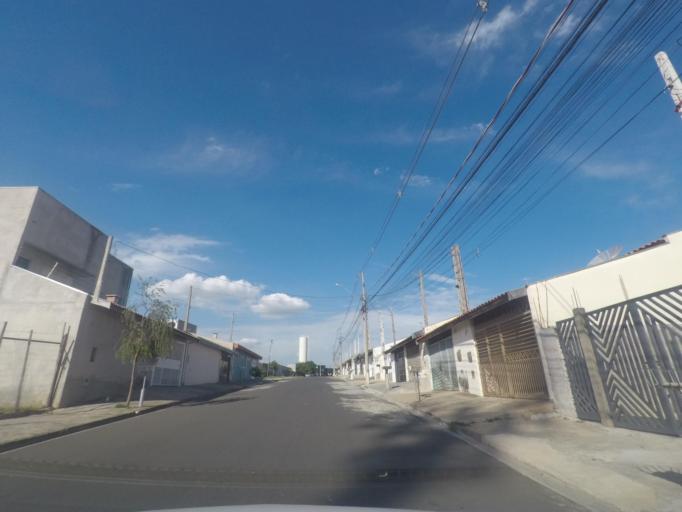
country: BR
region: Sao Paulo
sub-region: Sumare
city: Sumare
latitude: -22.8051
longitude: -47.2728
